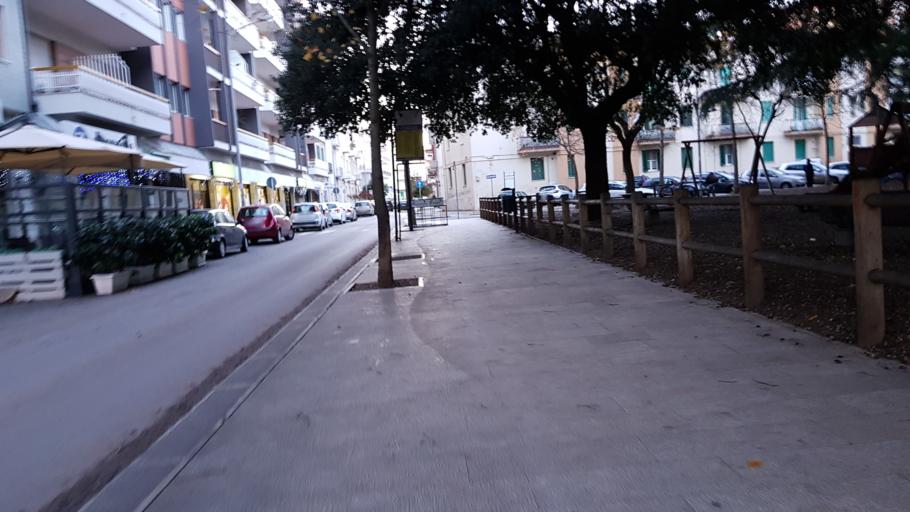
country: IT
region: Apulia
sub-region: Provincia di Bari
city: Gioia del Colle
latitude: 40.7951
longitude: 16.9224
